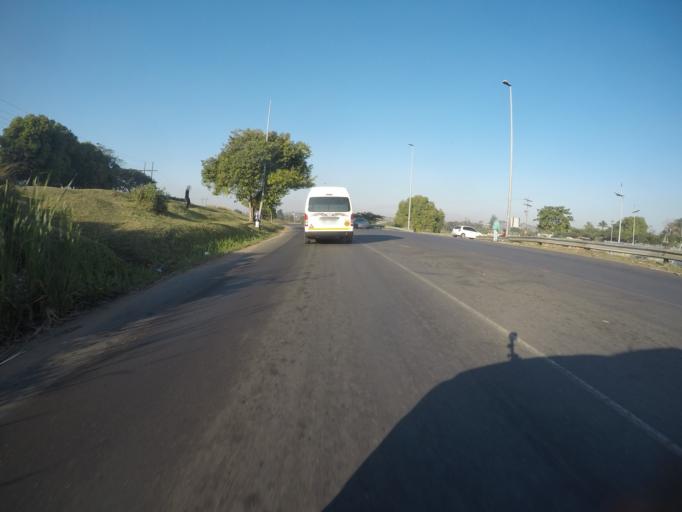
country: ZA
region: KwaZulu-Natal
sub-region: iLembe District Municipality
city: Stanger
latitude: -29.3889
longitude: 31.2509
